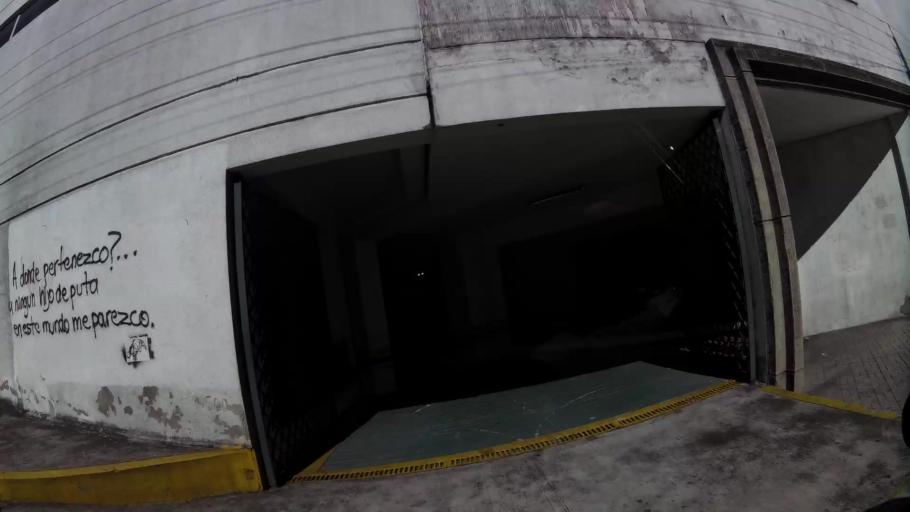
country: EC
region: Pichincha
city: Quito
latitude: -0.2257
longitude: -78.5215
